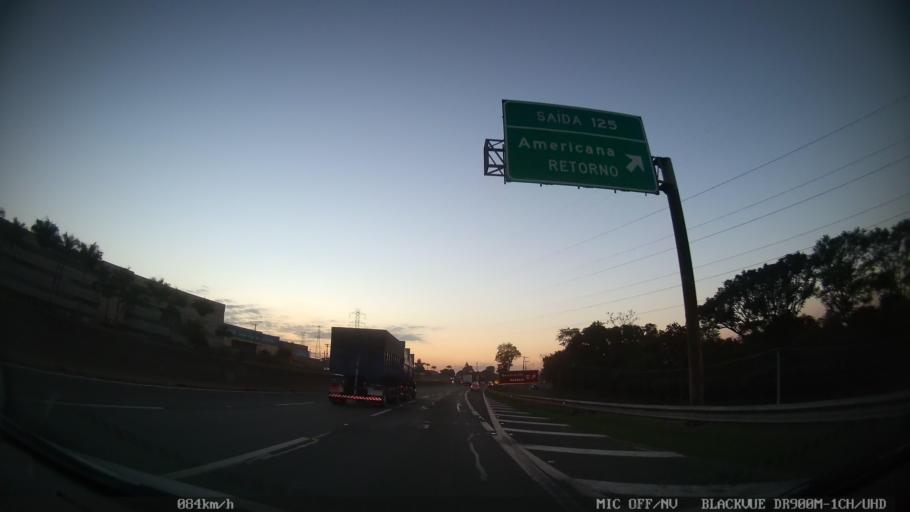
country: BR
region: Sao Paulo
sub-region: Americana
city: Americana
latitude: -22.7315
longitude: -47.2908
